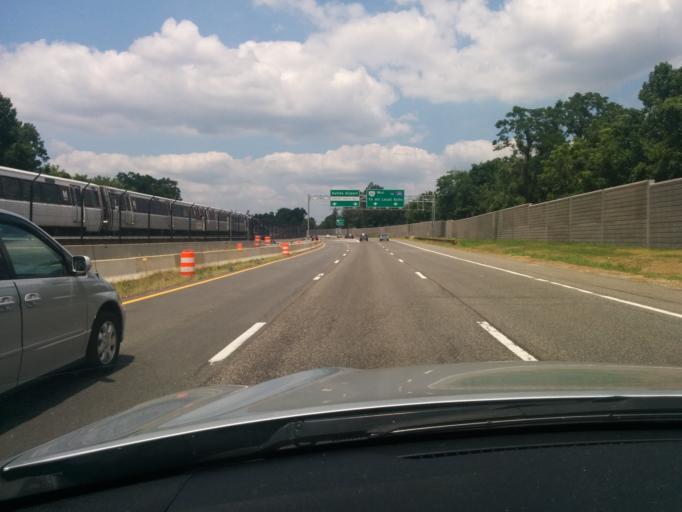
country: US
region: Virginia
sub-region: Fairfax County
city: Pimmit Hills
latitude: 38.9245
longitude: -77.1969
